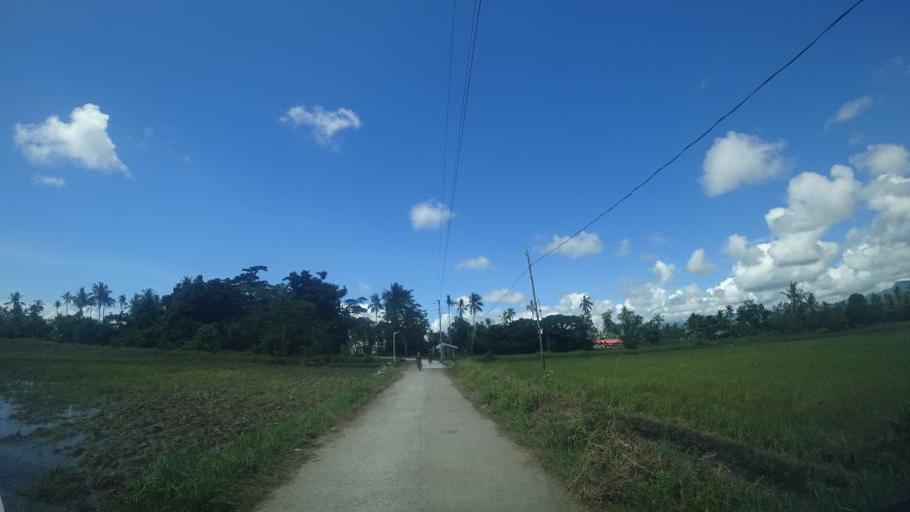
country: PH
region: Eastern Visayas
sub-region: Province of Leyte
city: Cabacungan
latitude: 10.9162
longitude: 124.9762
